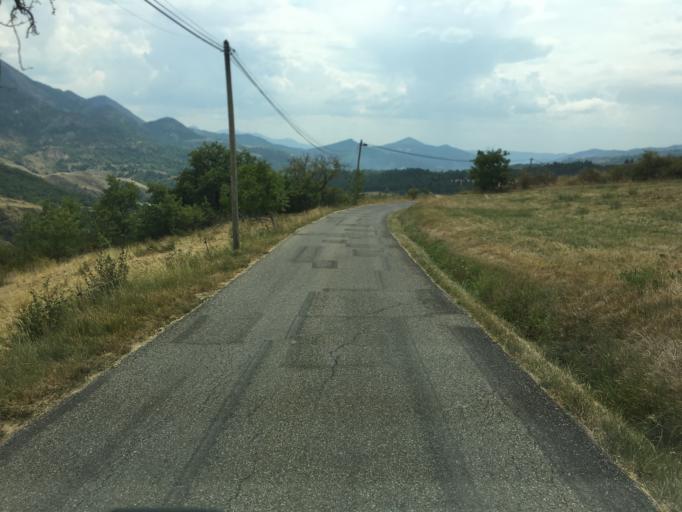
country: FR
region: Provence-Alpes-Cote d'Azur
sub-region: Departement des Alpes-de-Haute-Provence
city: Digne-les-Bains
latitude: 44.1883
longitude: 6.1420
